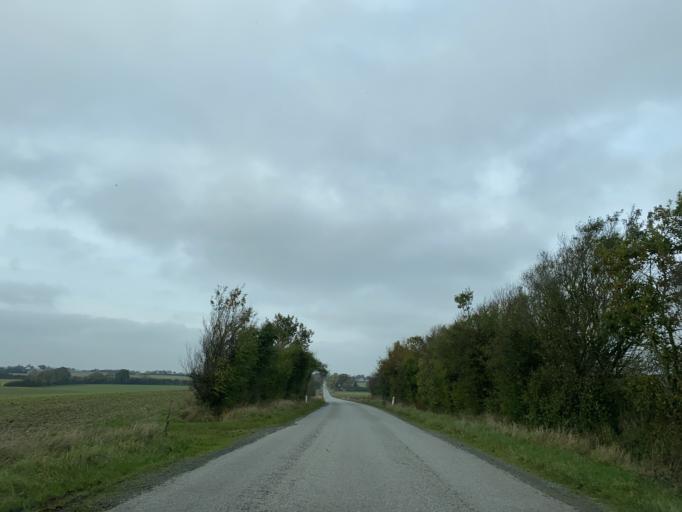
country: DK
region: South Denmark
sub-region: Haderslev Kommune
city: Starup
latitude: 55.1765
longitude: 9.5177
